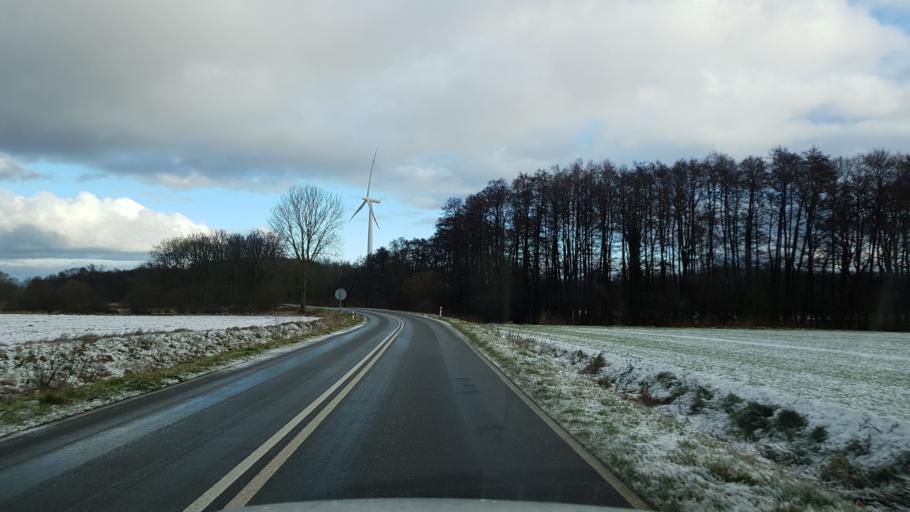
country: PL
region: West Pomeranian Voivodeship
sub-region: Powiat gryficki
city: Karnice
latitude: 54.0394
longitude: 15.0595
